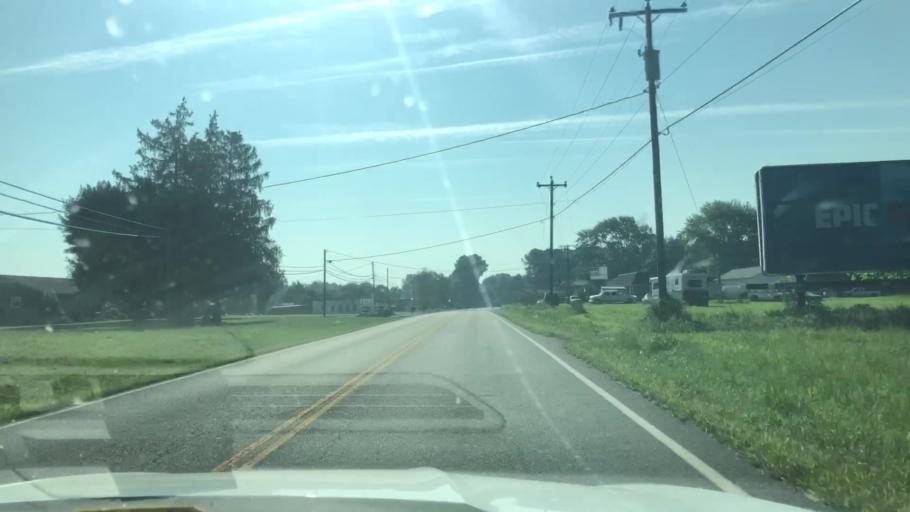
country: US
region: Virginia
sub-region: Richmond County
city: Warsaw
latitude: 37.8894
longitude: -76.6339
